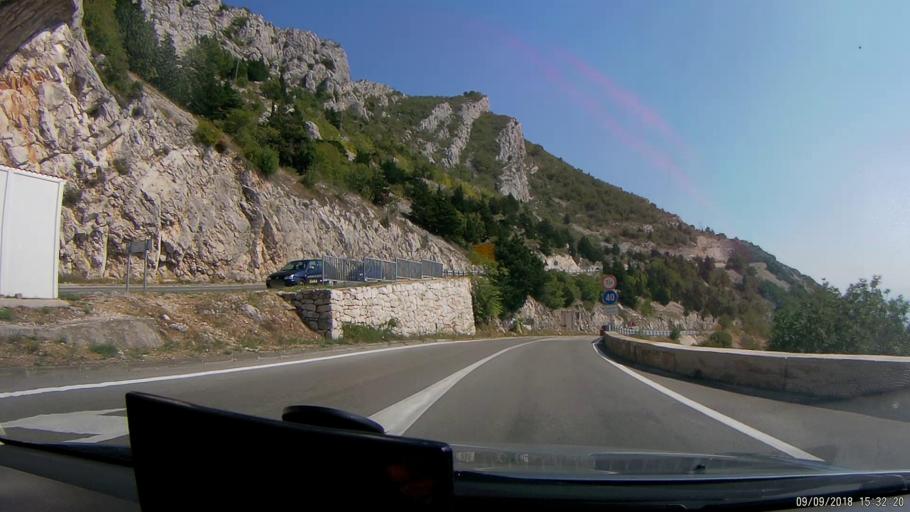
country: HR
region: Splitsko-Dalmatinska
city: Donja Brela
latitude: 43.4022
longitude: 16.8918
